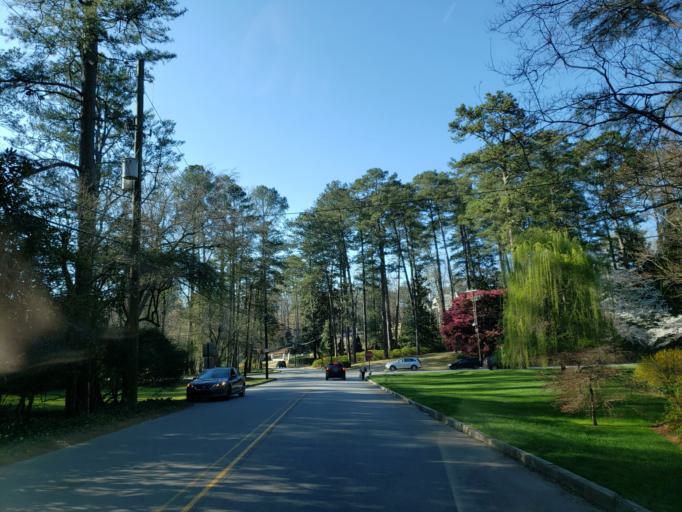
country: US
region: Georgia
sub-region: DeKalb County
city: North Atlanta
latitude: 33.8550
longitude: -84.3946
